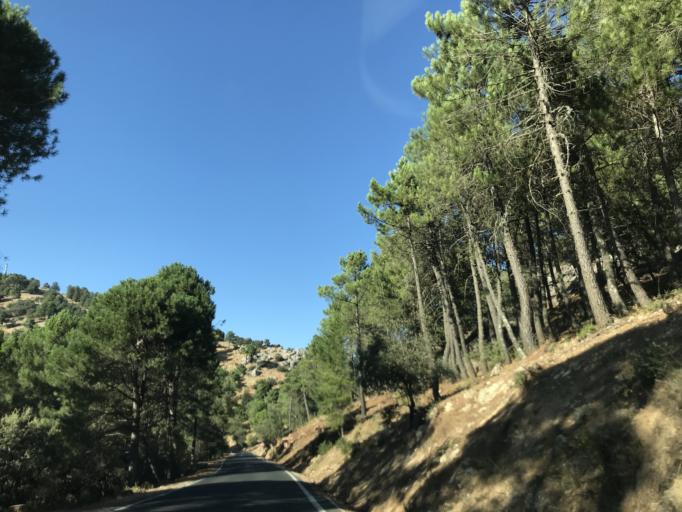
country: ES
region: Andalusia
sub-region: Provincia de Jaen
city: La Iruela
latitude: 37.9494
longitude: -2.9413
